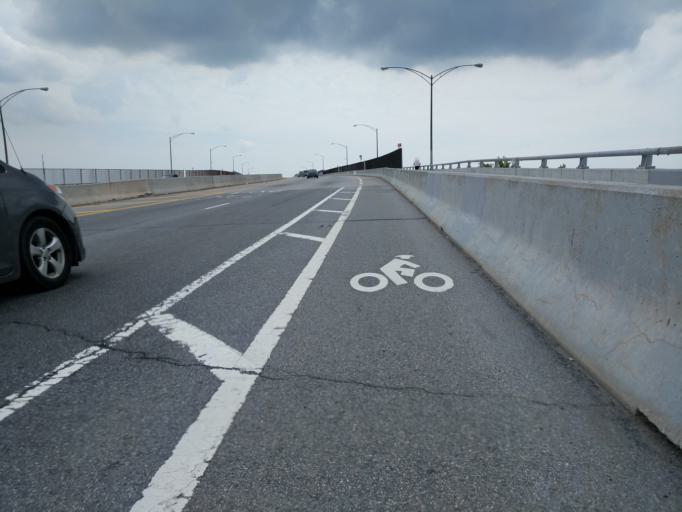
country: US
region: New York
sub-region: Queens County
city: Borough of Queens
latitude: 40.6463
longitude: -73.8368
